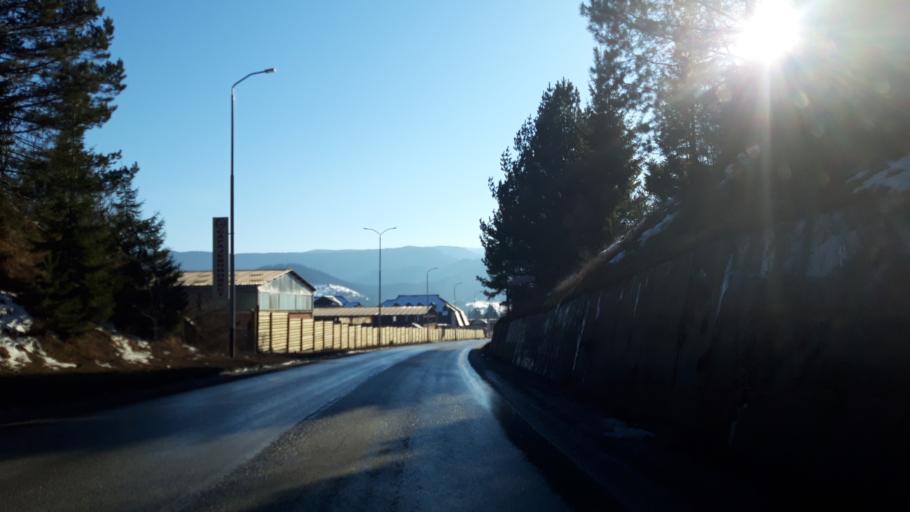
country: BA
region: Republika Srpska
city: Pale
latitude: 43.8260
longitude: 18.5592
